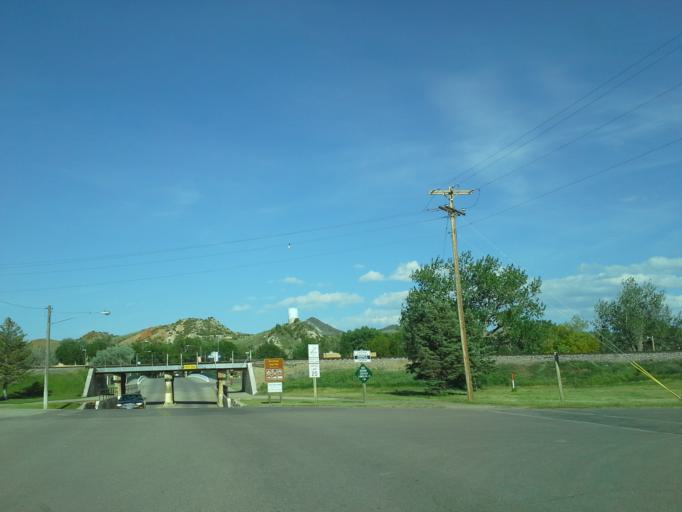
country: US
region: Wyoming
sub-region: Hot Springs County
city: Thermopolis
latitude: 43.6505
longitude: -108.2042
